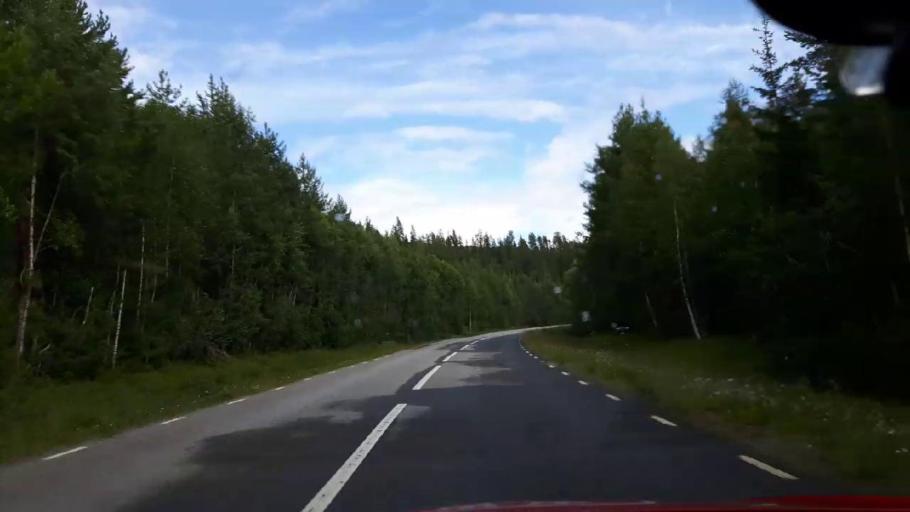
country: SE
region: Jaemtland
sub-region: Stroemsunds Kommun
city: Stroemsund
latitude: 64.3463
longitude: 15.0506
